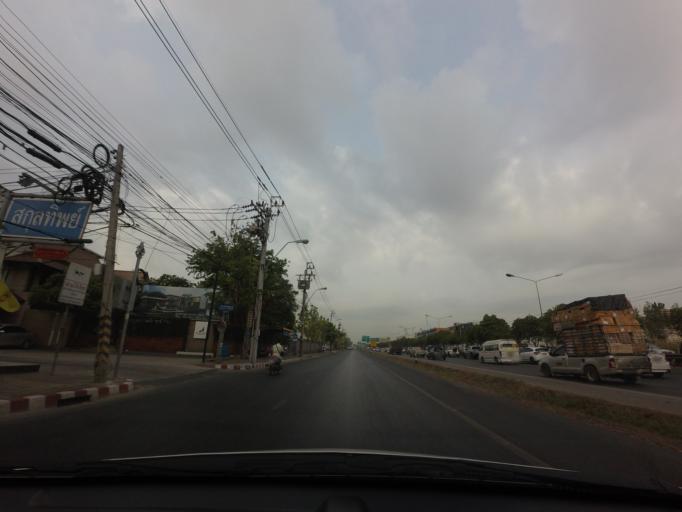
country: TH
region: Bangkok
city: Thawi Watthana
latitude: 13.7879
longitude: 100.3396
